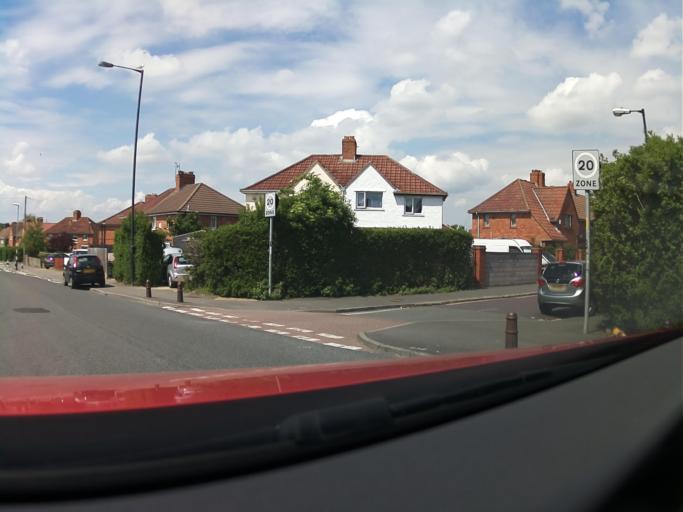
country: GB
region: England
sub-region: Bristol
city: Bristol
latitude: 51.4980
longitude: -2.5985
